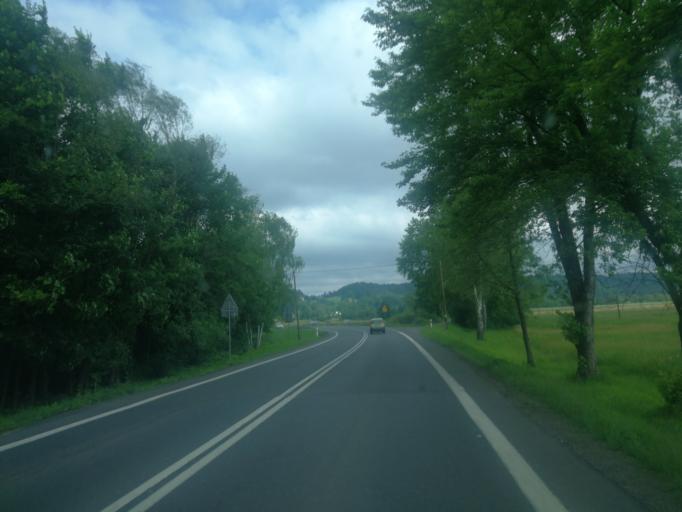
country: PL
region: Subcarpathian Voivodeship
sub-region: Powiat leski
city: Lesko
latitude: 49.4904
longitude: 22.3209
